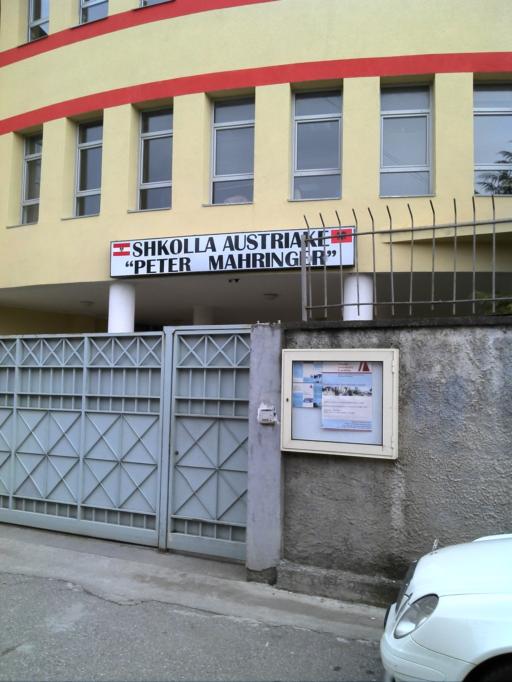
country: AL
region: Shkoder
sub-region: Rrethi i Shkodres
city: Shkoder
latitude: 42.0588
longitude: 19.5170
